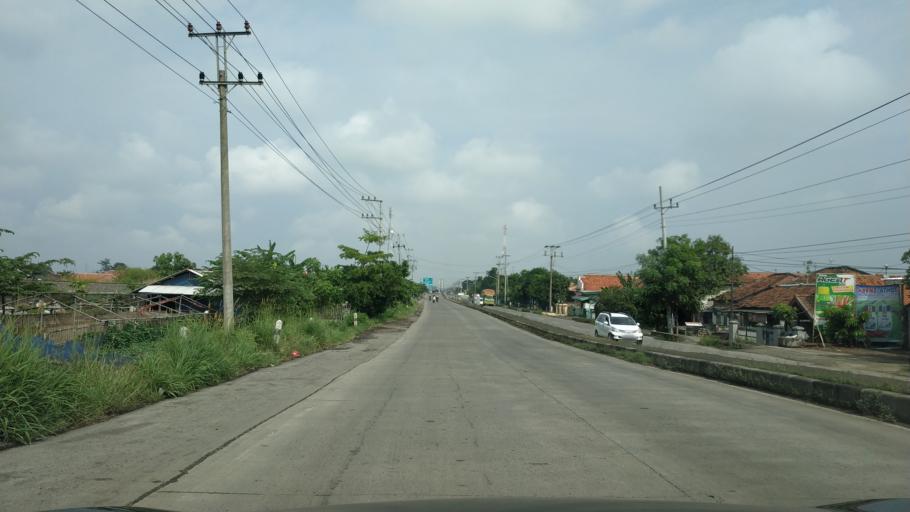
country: ID
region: Central Java
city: Bulakamba
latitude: -6.8716
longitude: 108.8911
